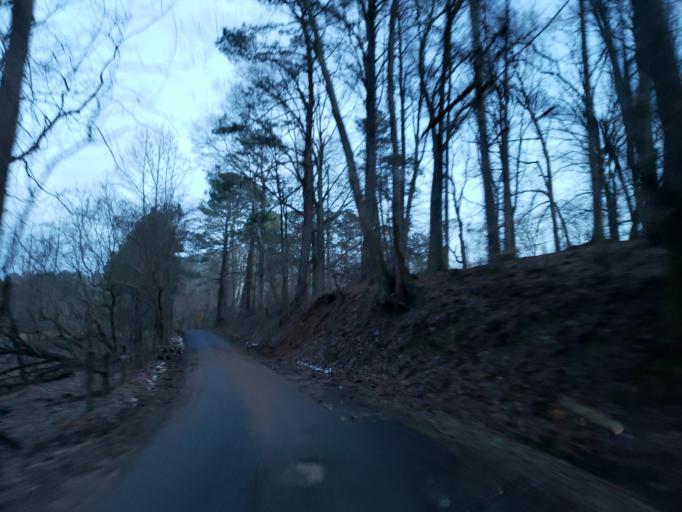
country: US
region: Georgia
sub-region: Cherokee County
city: Ball Ground
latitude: 34.2929
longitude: -84.2827
